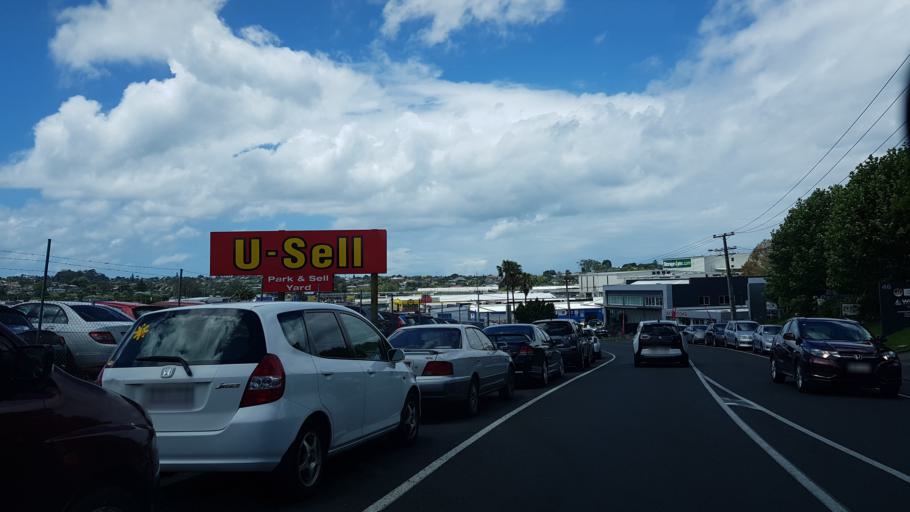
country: NZ
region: Auckland
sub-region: Auckland
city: North Shore
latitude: -36.7754
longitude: 174.7368
